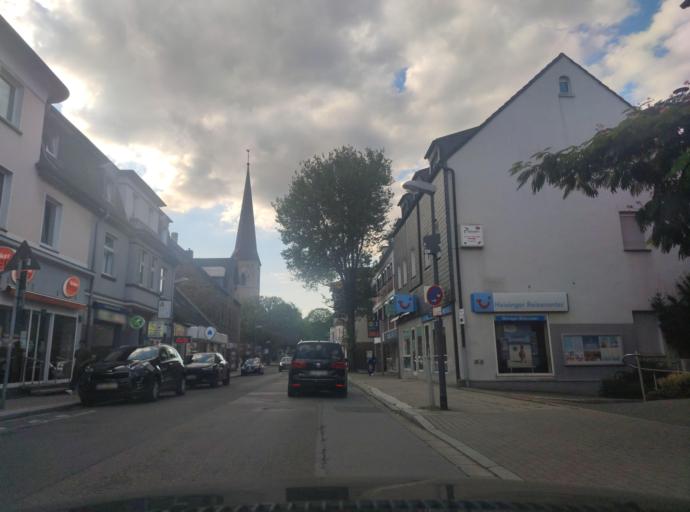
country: DE
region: North Rhine-Westphalia
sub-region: Regierungsbezirk Dusseldorf
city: Velbert
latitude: 51.4036
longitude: 7.0666
